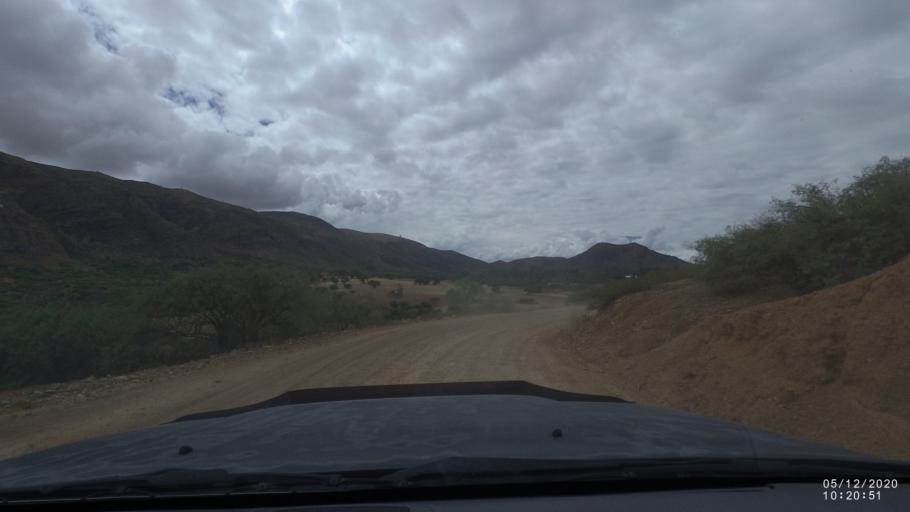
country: BO
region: Cochabamba
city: Sipe Sipe
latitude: -17.4860
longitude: -66.2826
